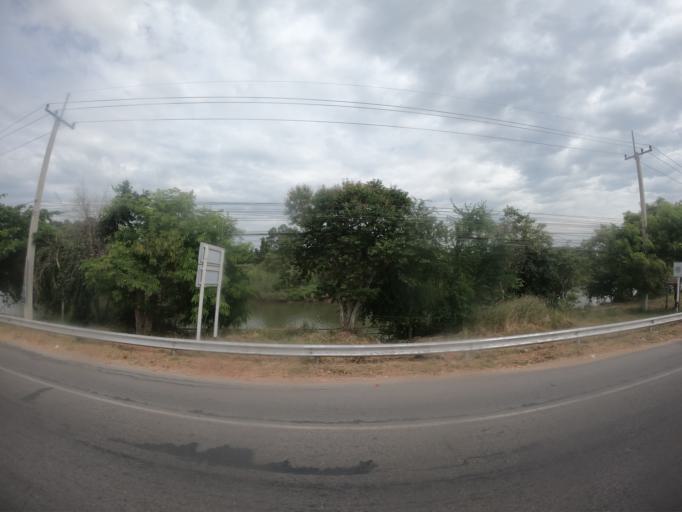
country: TH
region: Maha Sarakham
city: Maha Sarakham
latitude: 16.2181
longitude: 103.2762
